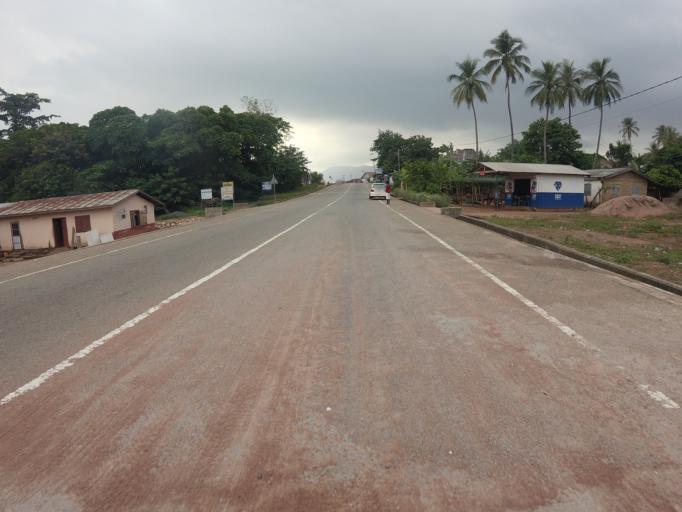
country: GH
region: Volta
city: Ho
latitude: 6.7717
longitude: 0.4801
